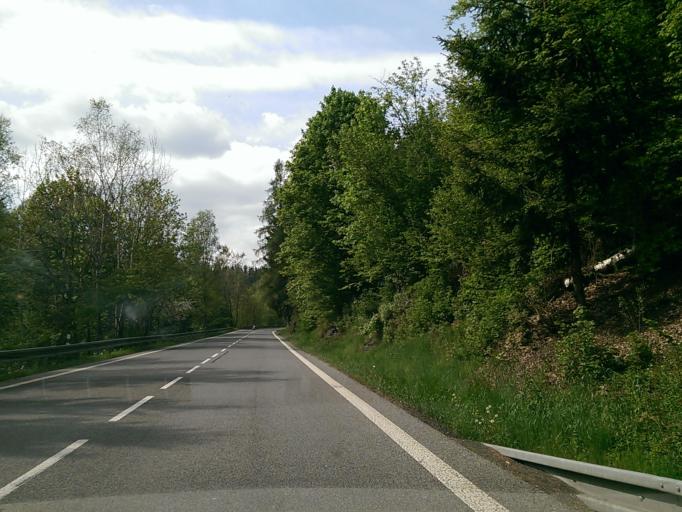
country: CZ
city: Pencin
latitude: 50.6758
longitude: 15.2677
